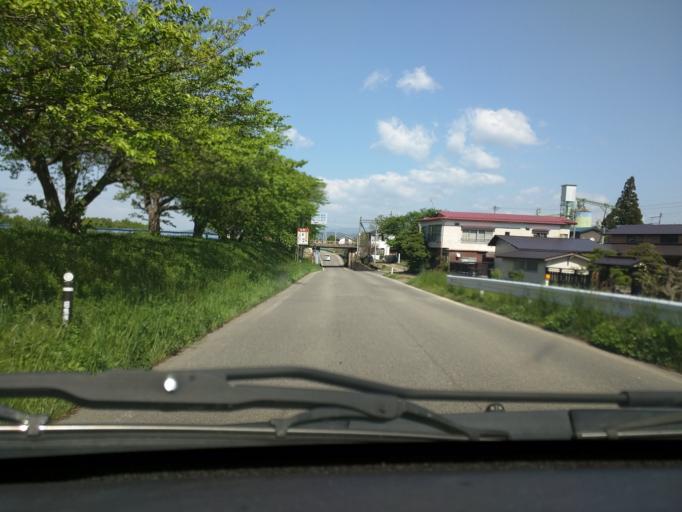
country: JP
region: Fukushima
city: Kitakata
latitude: 37.5912
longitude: 139.8885
